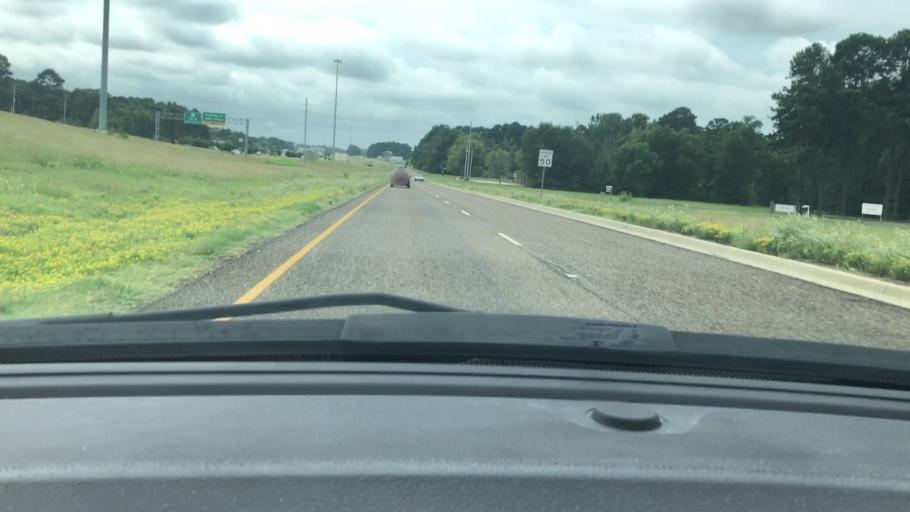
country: US
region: Texas
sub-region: Bowie County
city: Wake Village
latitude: 33.4419
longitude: -94.0975
